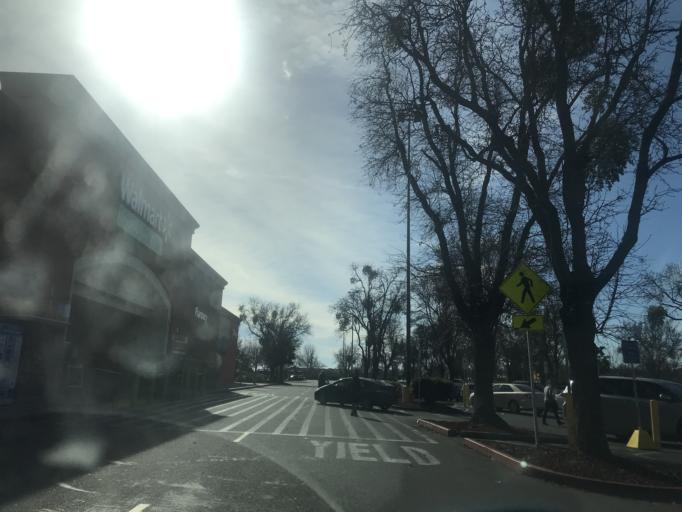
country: US
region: California
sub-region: Yolo County
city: Woodland
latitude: 38.6616
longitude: -121.7641
